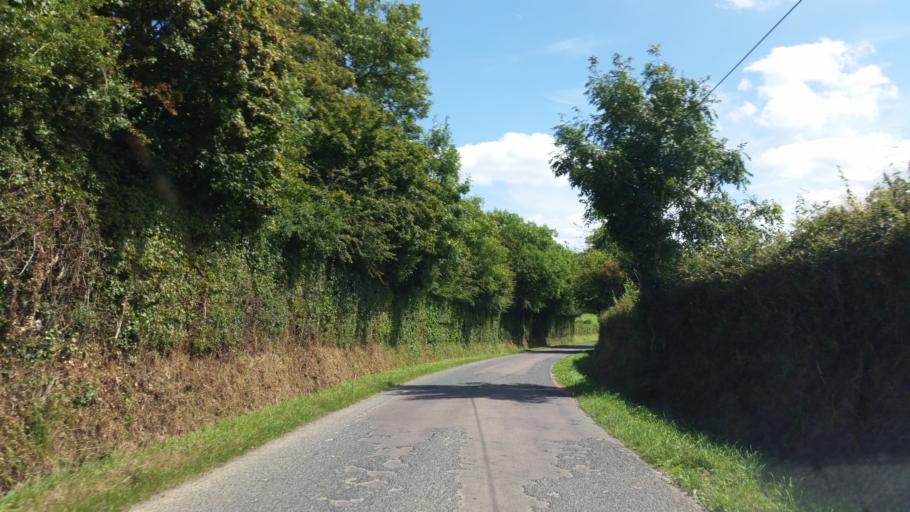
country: FR
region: Lower Normandy
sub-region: Departement de la Manche
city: Montebourg
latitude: 49.4634
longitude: -1.3327
